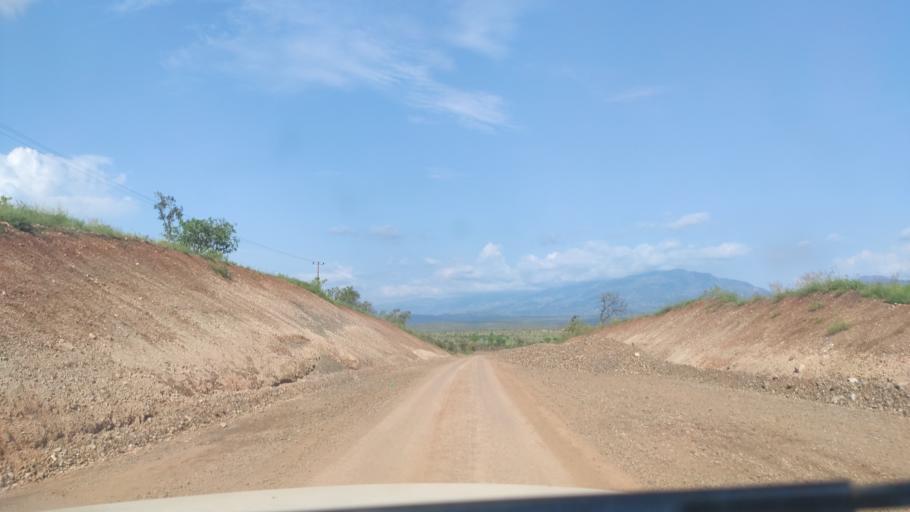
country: ET
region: Southern Nations, Nationalities, and People's Region
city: Felege Neway
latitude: 6.4256
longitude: 37.2240
